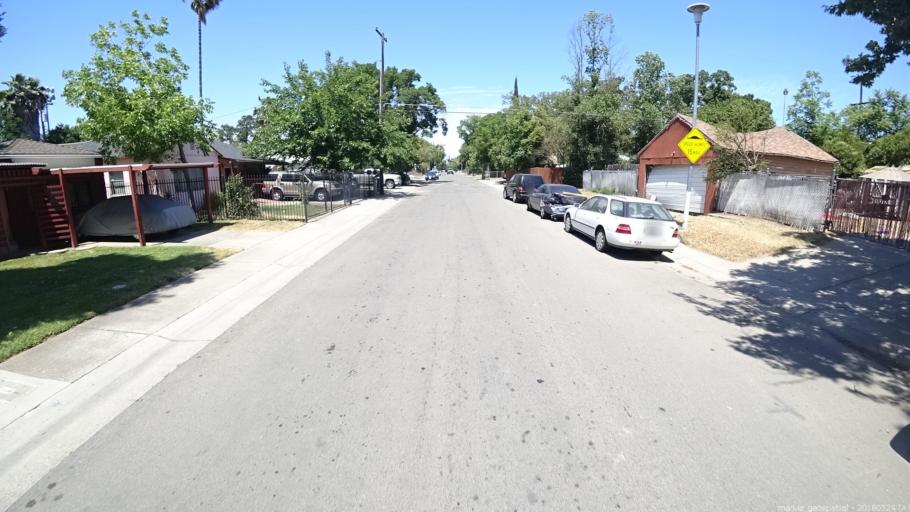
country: US
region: California
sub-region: Sacramento County
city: Sacramento
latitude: 38.6094
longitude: -121.4643
